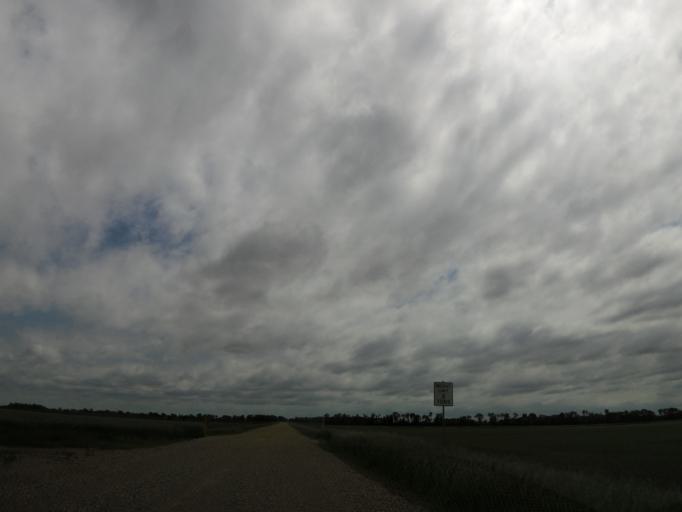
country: US
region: North Dakota
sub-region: Walsh County
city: Grafton
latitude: 48.4330
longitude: -97.4918
